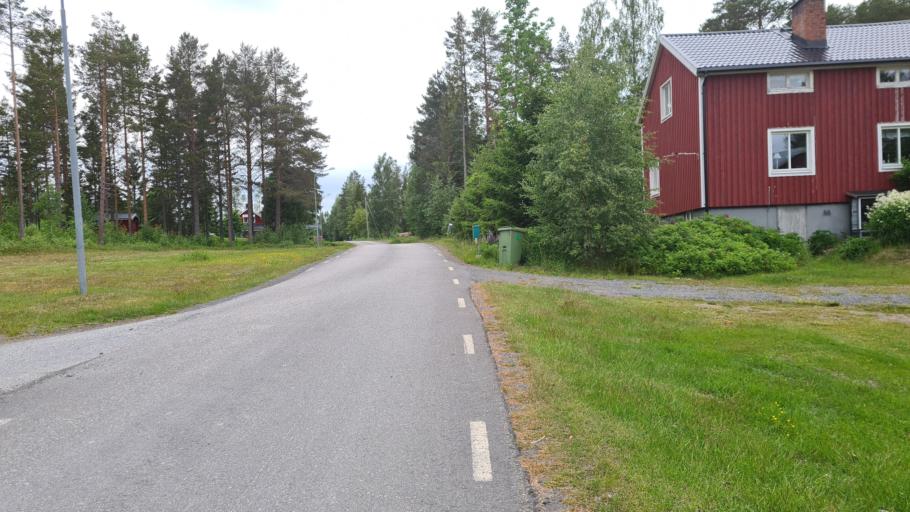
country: SE
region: Vaesternorrland
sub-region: Kramfors Kommun
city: Nordingra
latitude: 62.9729
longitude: 18.4253
